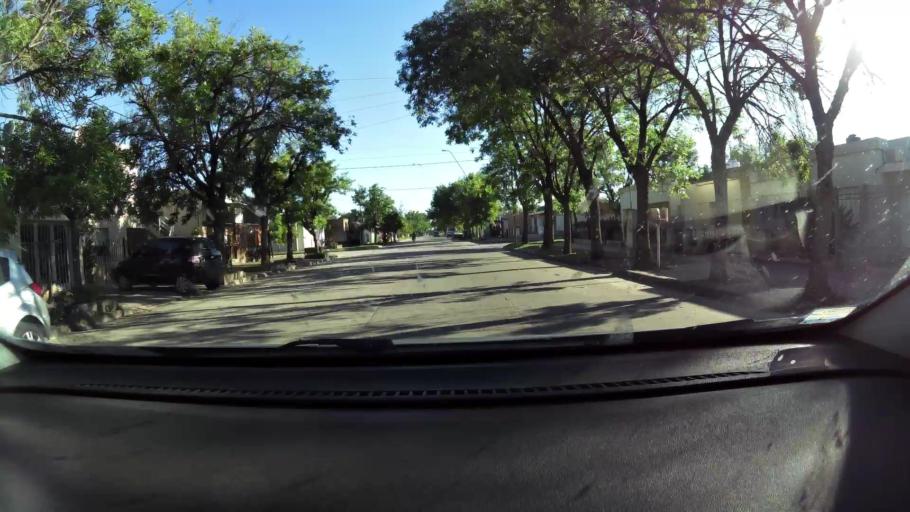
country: AR
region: Cordoba
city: San Francisco
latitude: -31.4419
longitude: -62.0947
